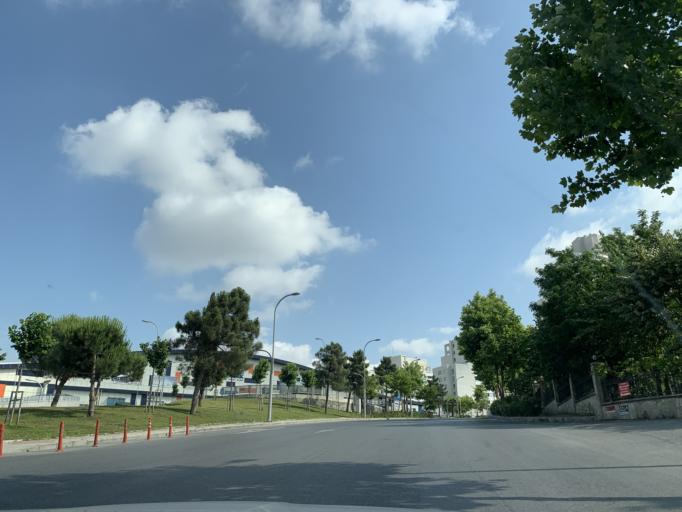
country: TR
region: Istanbul
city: Esenyurt
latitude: 41.0814
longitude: 28.6777
